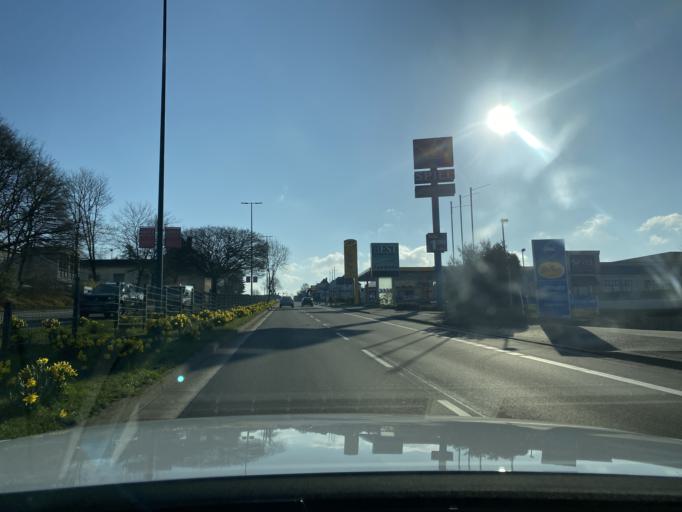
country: DE
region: North Rhine-Westphalia
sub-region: Regierungsbezirk Dusseldorf
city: Remscheid
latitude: 51.1774
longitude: 7.2117
